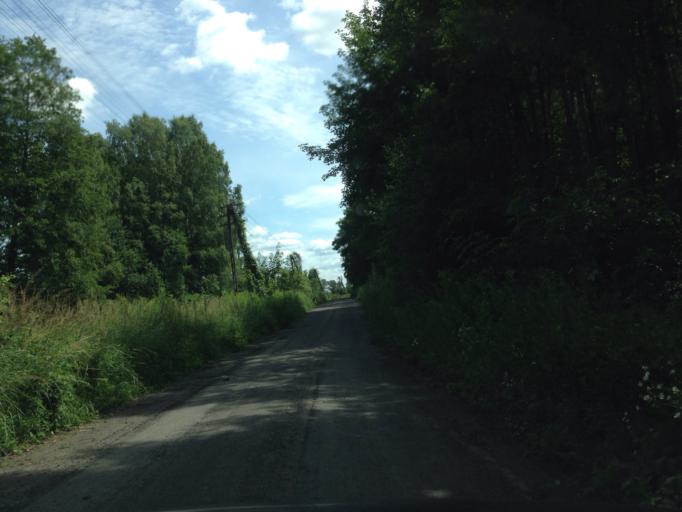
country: PL
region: Kujawsko-Pomorskie
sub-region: Powiat brodnicki
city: Bartniczka
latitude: 53.2656
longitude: 19.5817
